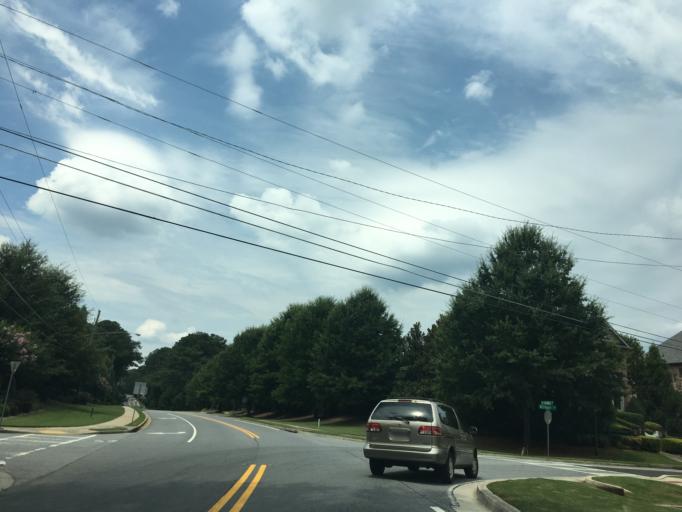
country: US
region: Georgia
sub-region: Fulton County
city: Alpharetta
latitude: 34.0871
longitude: -84.3260
